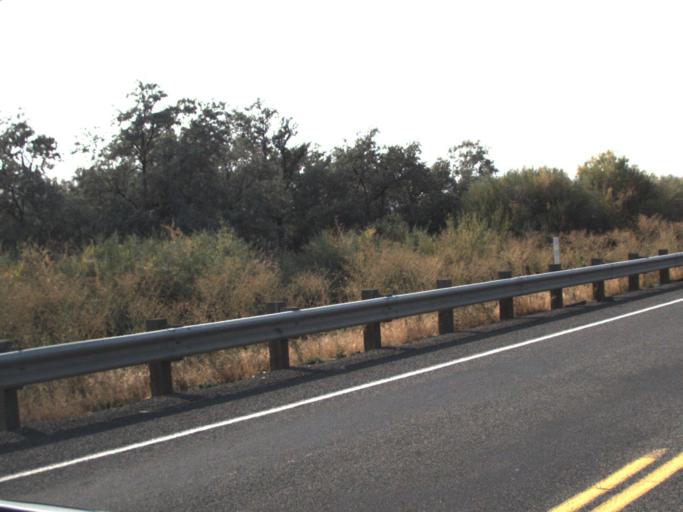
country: US
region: Washington
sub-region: Yakima County
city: Granger
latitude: 46.3099
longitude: -120.2095
